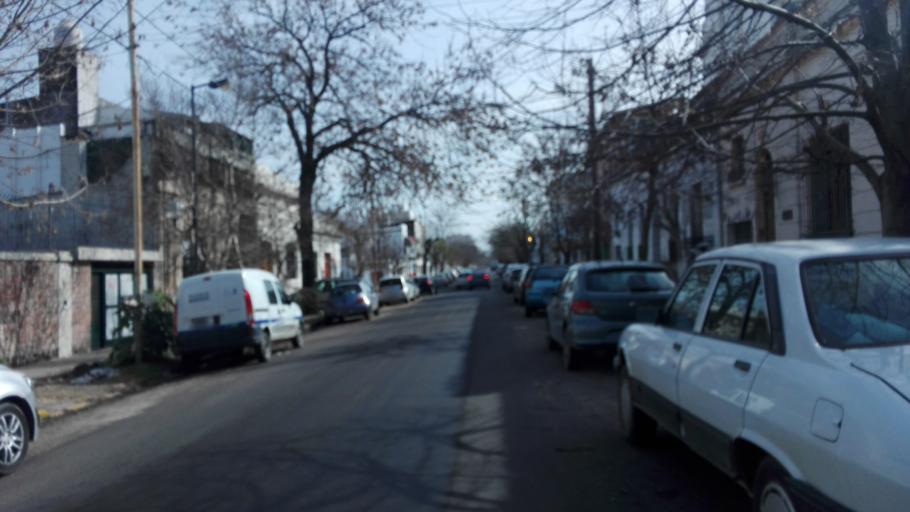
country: AR
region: Buenos Aires
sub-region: Partido de La Plata
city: La Plata
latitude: -34.9265
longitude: -57.9570
